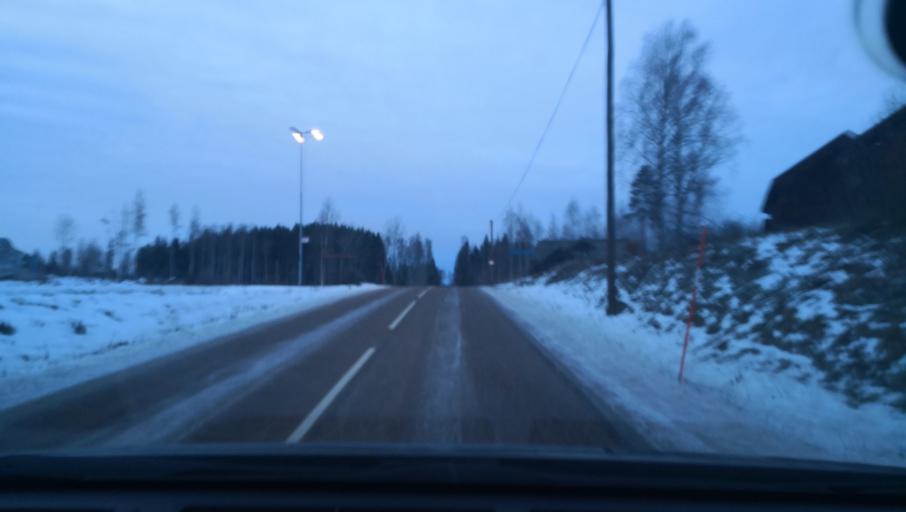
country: SE
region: Dalarna
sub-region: Avesta Kommun
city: Horndal
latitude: 60.1919
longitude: 16.4677
